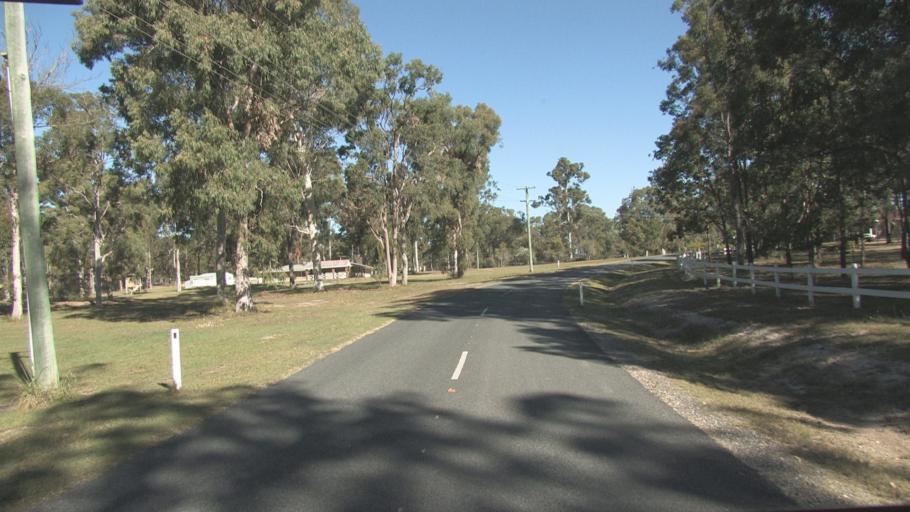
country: AU
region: Queensland
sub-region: Logan
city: Logan Reserve
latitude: -27.7354
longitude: 153.1227
